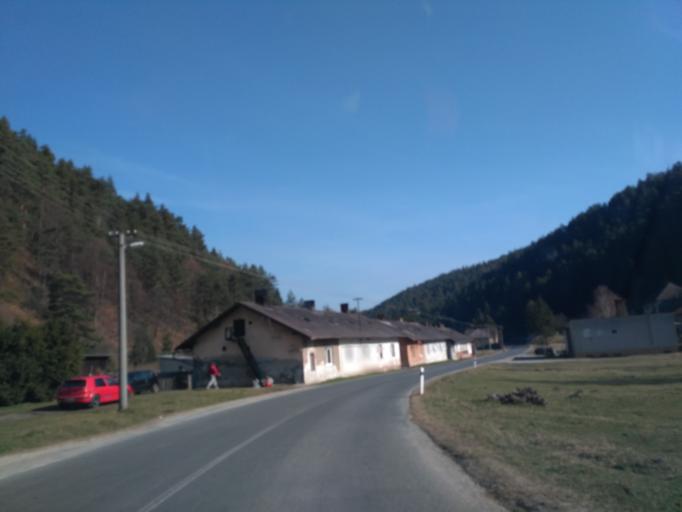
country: SK
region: Kosicky
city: Medzev
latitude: 48.7469
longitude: 20.7750
